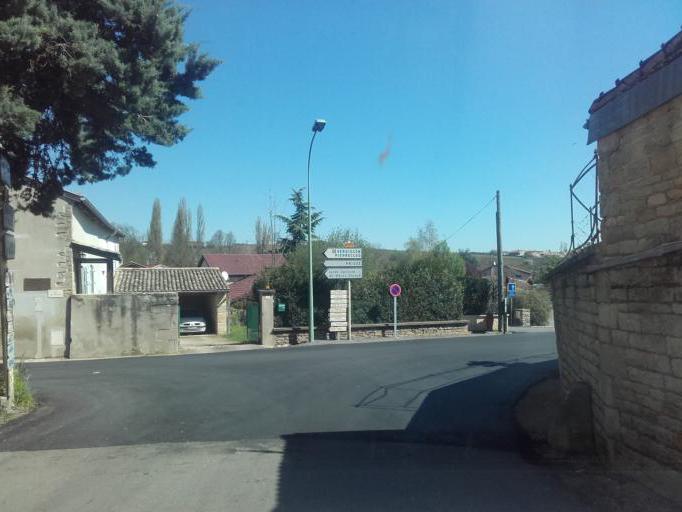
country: FR
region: Bourgogne
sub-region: Departement de Saone-et-Loire
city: Prisse
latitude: 46.3013
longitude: 4.7457
